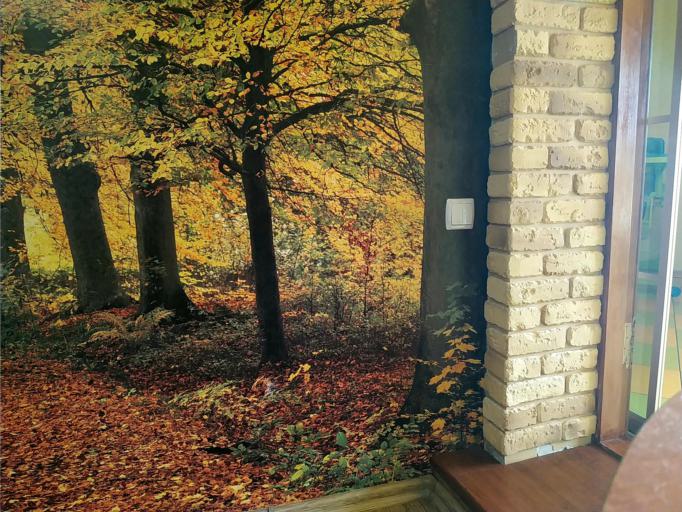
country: RU
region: Smolensk
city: Safonovo
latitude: 55.1138
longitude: 33.1813
